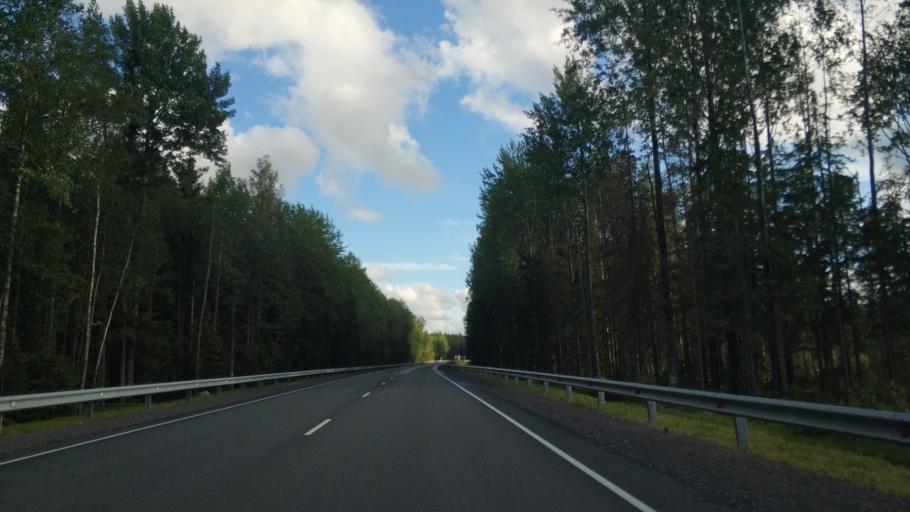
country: RU
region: Leningrad
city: Priozersk
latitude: 60.9129
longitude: 30.1575
